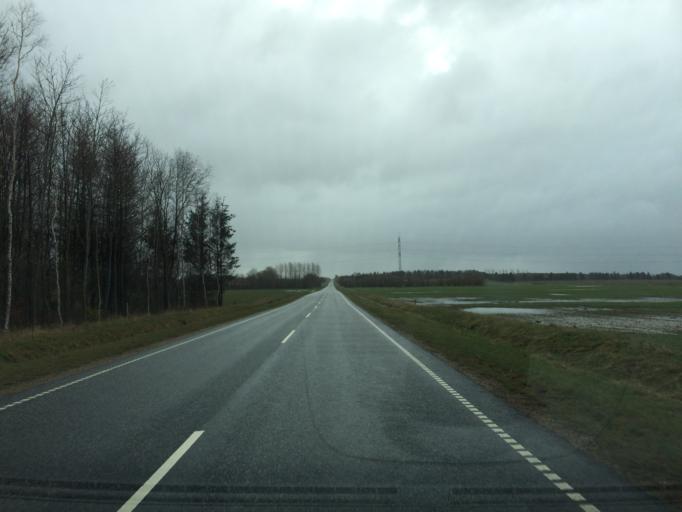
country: DK
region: Central Jutland
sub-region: Ringkobing-Skjern Kommune
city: Videbaek
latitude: 56.1895
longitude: 8.6010
